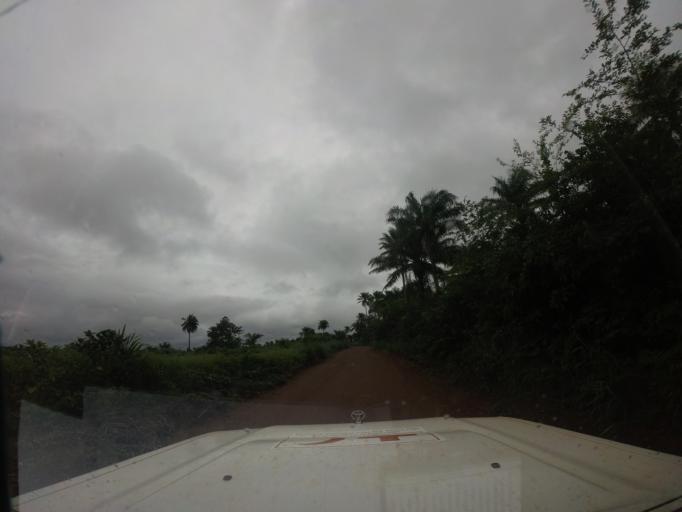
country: SL
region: Northern Province
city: Kambia
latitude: 9.1488
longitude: -12.8800
